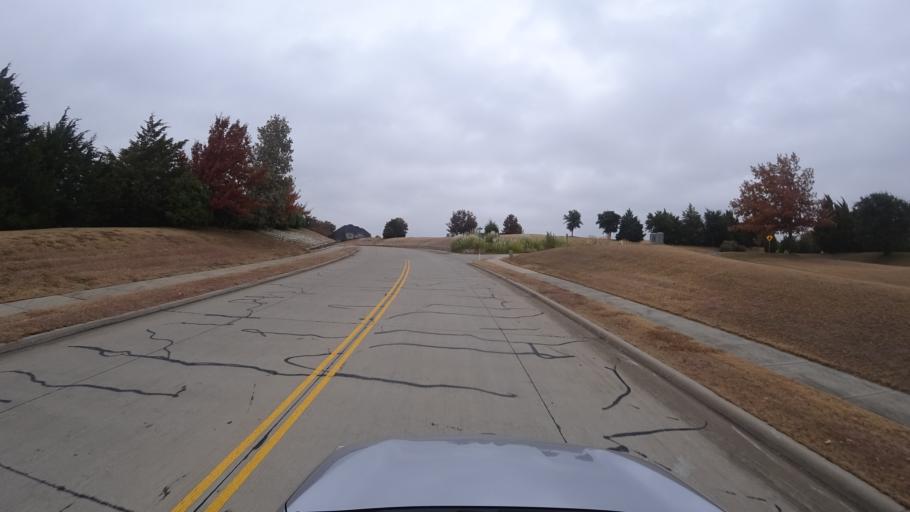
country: US
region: Texas
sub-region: Denton County
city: Lewisville
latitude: 33.0299
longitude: -96.9332
